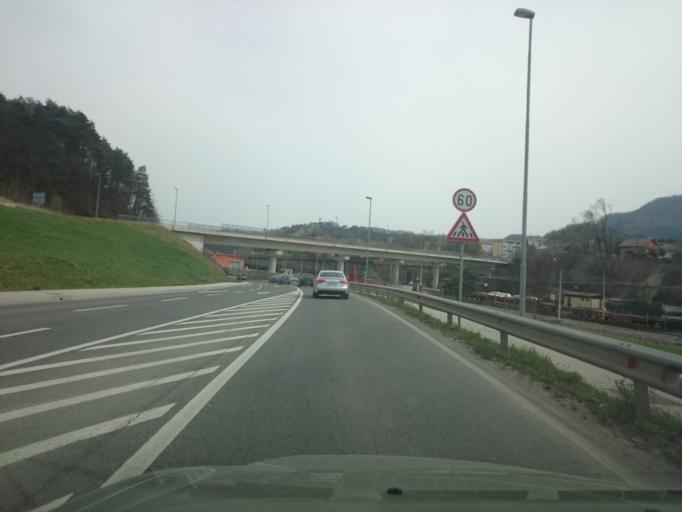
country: SI
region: Store
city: Store
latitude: 46.2250
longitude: 15.3091
